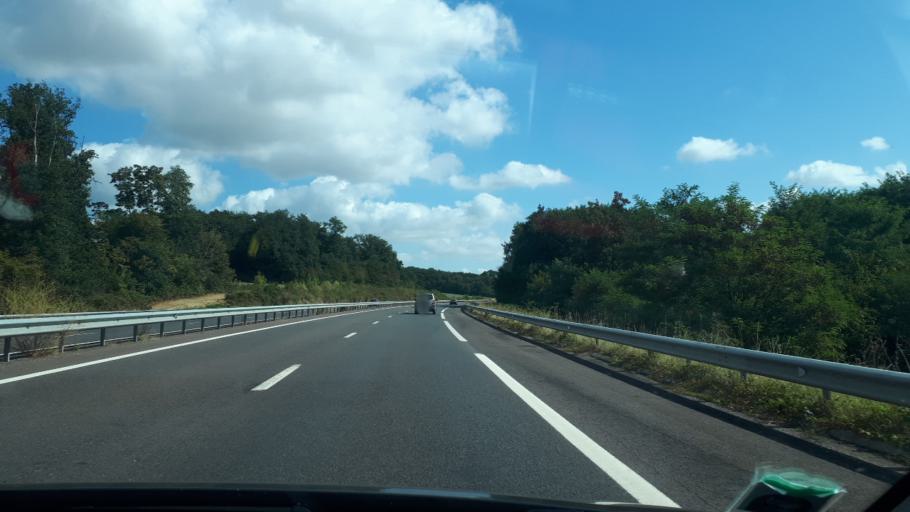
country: FR
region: Centre
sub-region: Departement du Loir-et-Cher
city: Saint-Ouen
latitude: 47.8559
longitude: 1.1089
